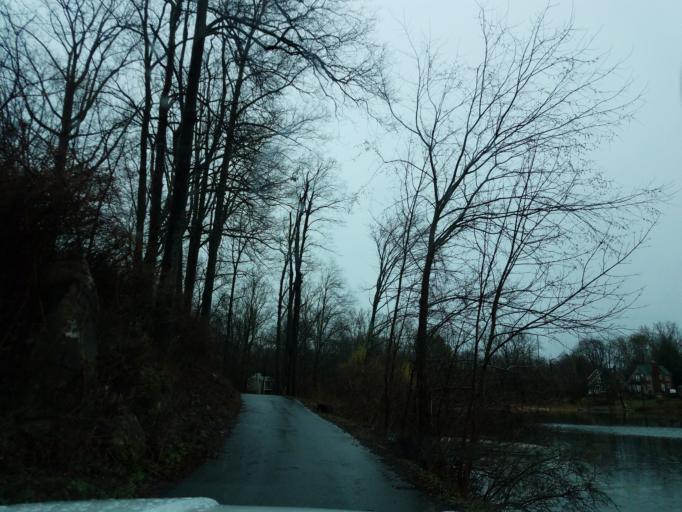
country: US
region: Connecticut
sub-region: Fairfield County
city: Ridgefield
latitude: 41.3398
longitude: -73.4935
